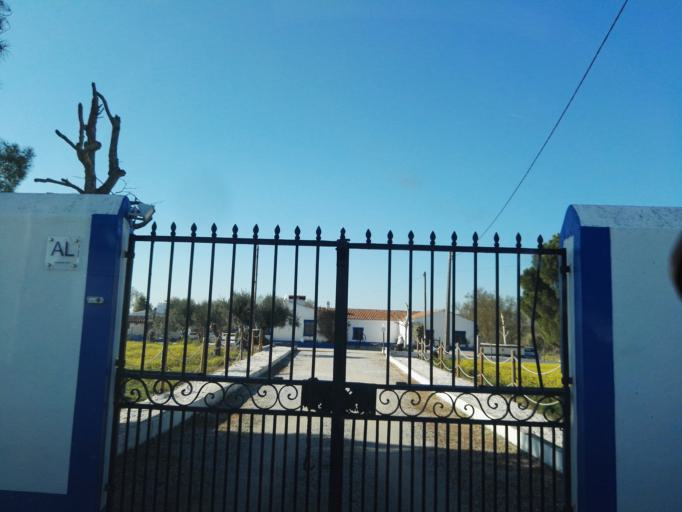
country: PT
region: Evora
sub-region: Evora
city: Evora
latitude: 38.5458
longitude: -7.9518
